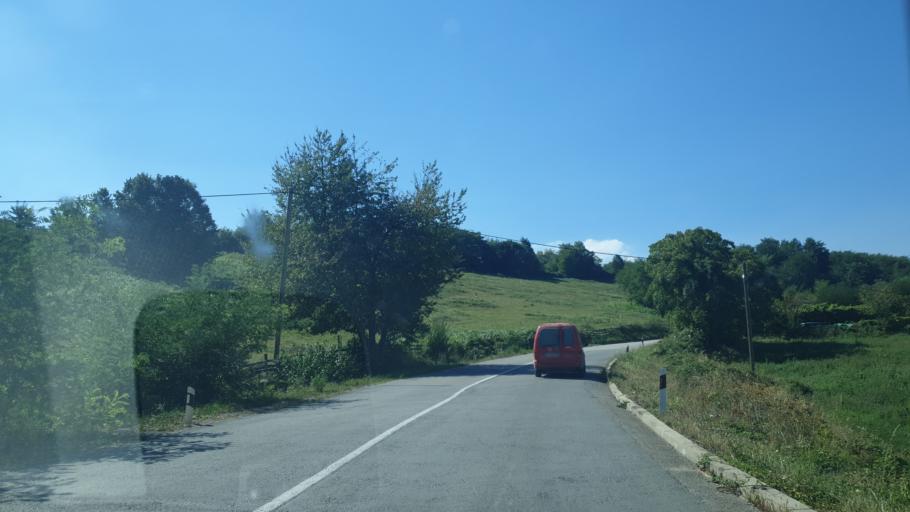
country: RS
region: Central Serbia
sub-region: Kolubarski Okrug
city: Mionica
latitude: 44.1810
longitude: 20.0559
